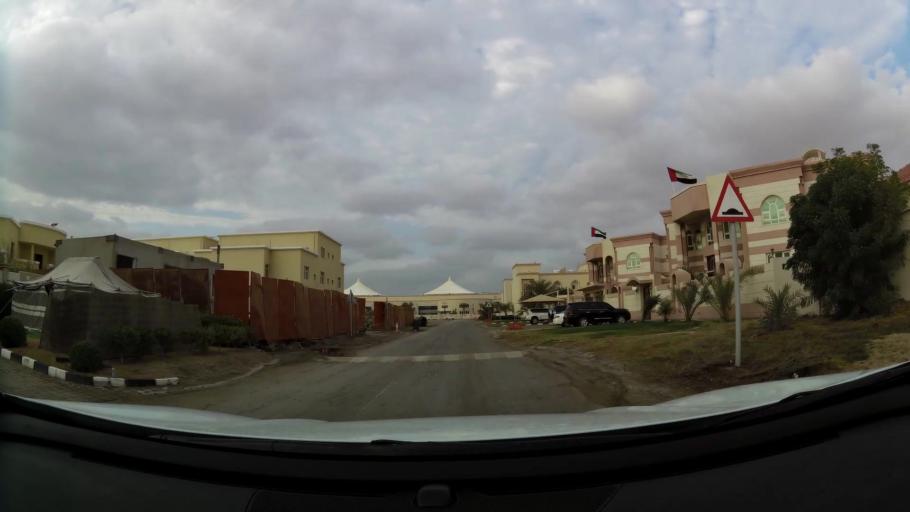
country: AE
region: Abu Dhabi
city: Abu Dhabi
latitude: 24.3588
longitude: 54.5529
